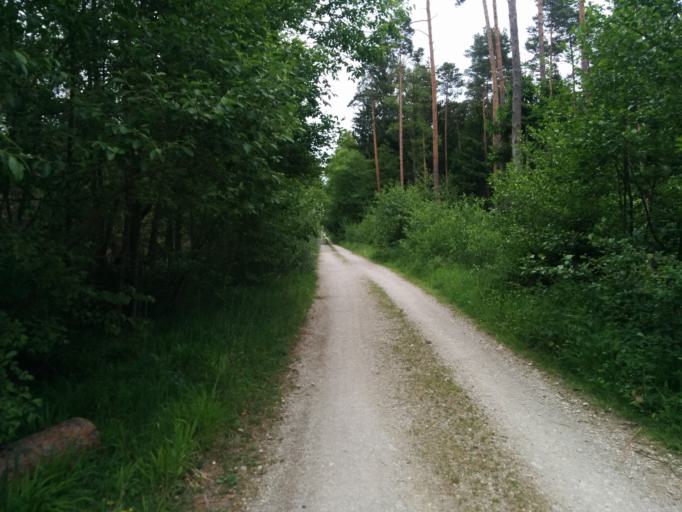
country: DE
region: Bavaria
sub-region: Regierungsbezirk Mittelfranken
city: Buckenhof
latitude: 49.5500
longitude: 11.0575
